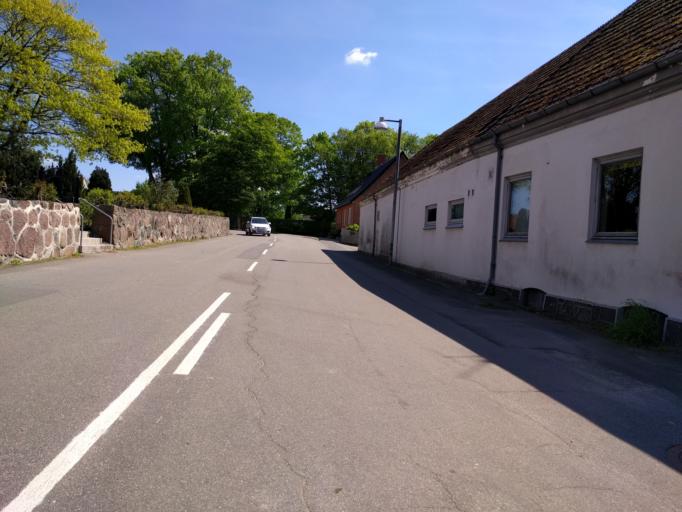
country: DK
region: Zealand
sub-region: Guldborgsund Kommune
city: Nykobing Falster
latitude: 54.7420
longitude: 11.9577
